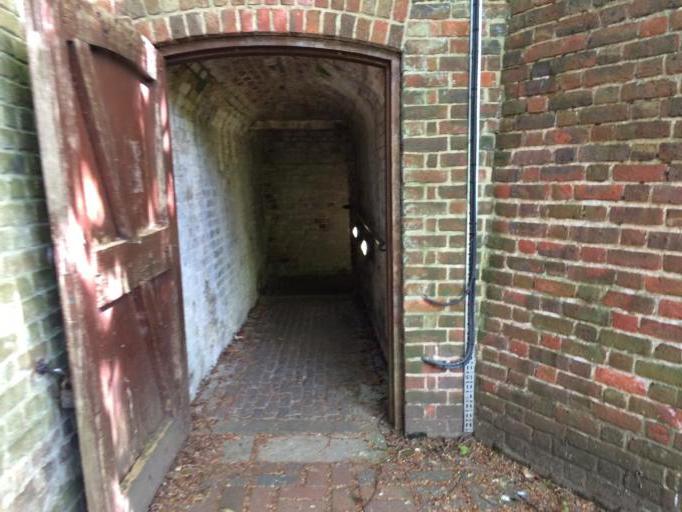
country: GB
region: England
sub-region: Greater London
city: Brentford
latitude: 51.4816
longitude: -0.2916
